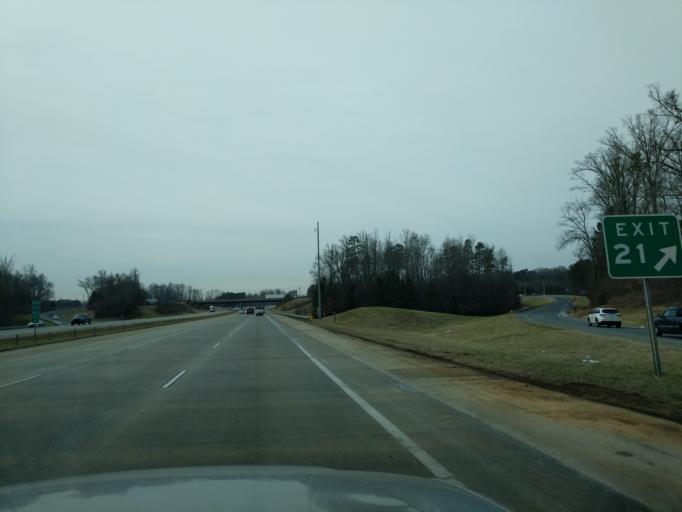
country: US
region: North Carolina
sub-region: Mecklenburg County
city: Huntersville
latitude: 35.3546
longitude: -80.8616
